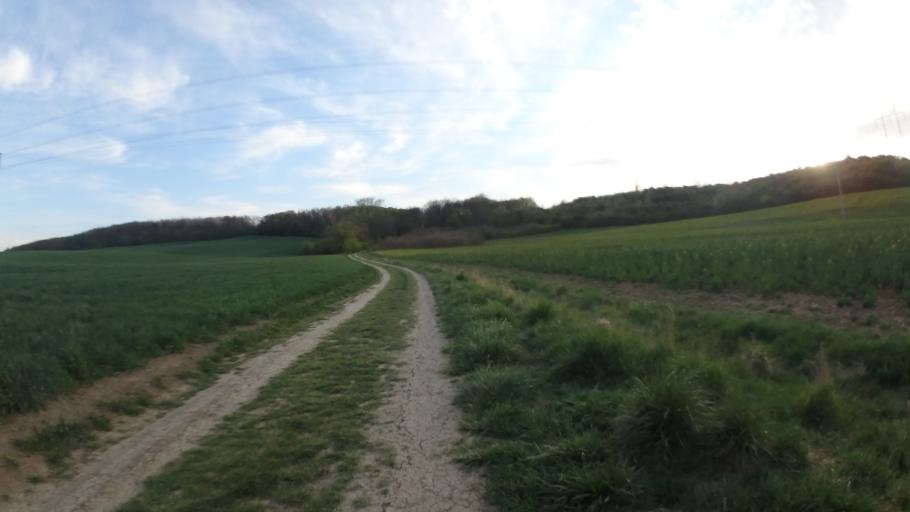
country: CZ
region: South Moravian
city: Moravany
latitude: 49.1413
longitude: 16.5675
